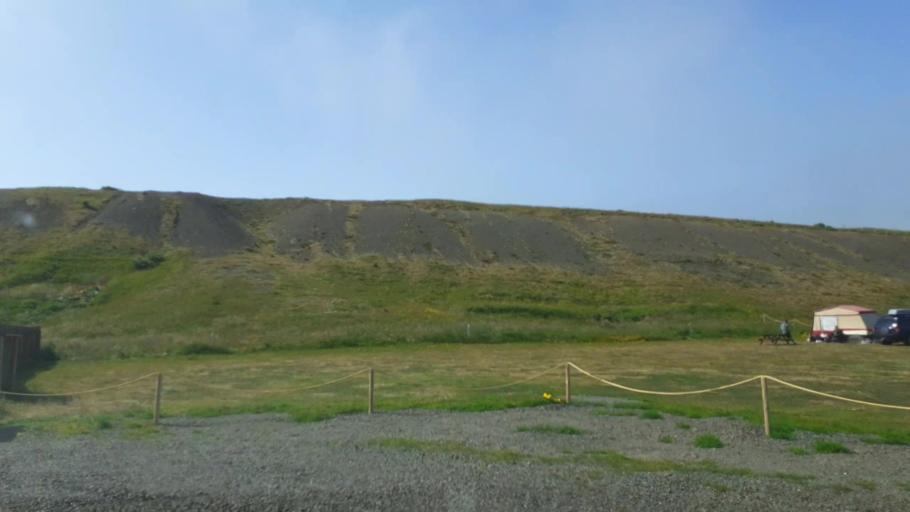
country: IS
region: West
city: Borgarnes
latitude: 65.2113
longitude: -21.0961
